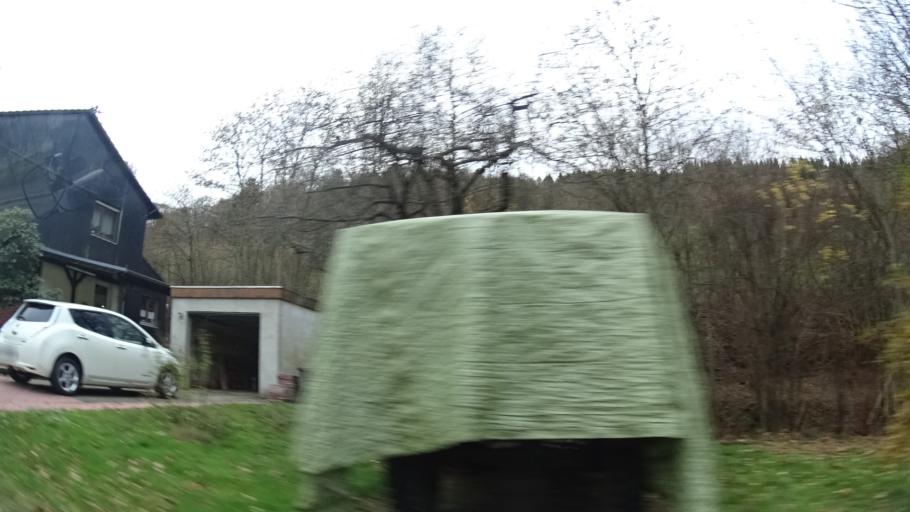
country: DE
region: Baden-Wuerttemberg
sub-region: Karlsruhe Region
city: Eberbach
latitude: 49.4285
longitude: 8.9565
